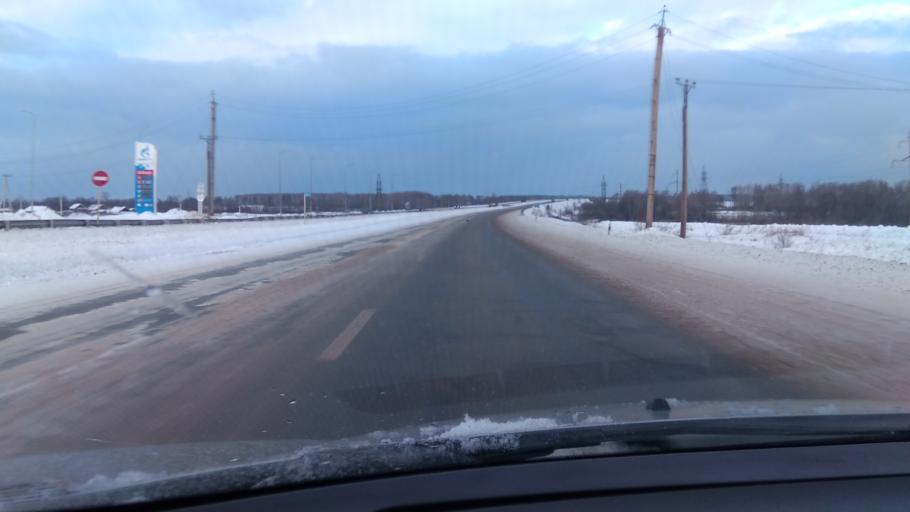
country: RU
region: Sverdlovsk
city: Tsementnyy
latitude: 57.4973
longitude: 60.1749
